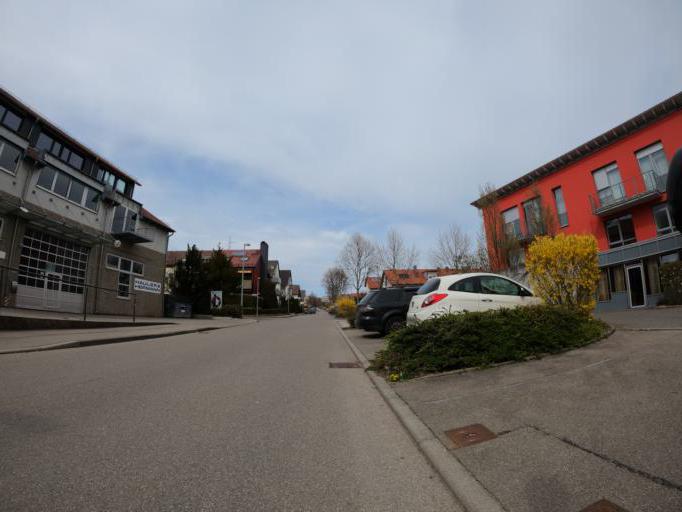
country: DE
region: Baden-Wuerttemberg
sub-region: Regierungsbezirk Stuttgart
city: Wolfschlugen
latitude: 48.6484
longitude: 9.2531
